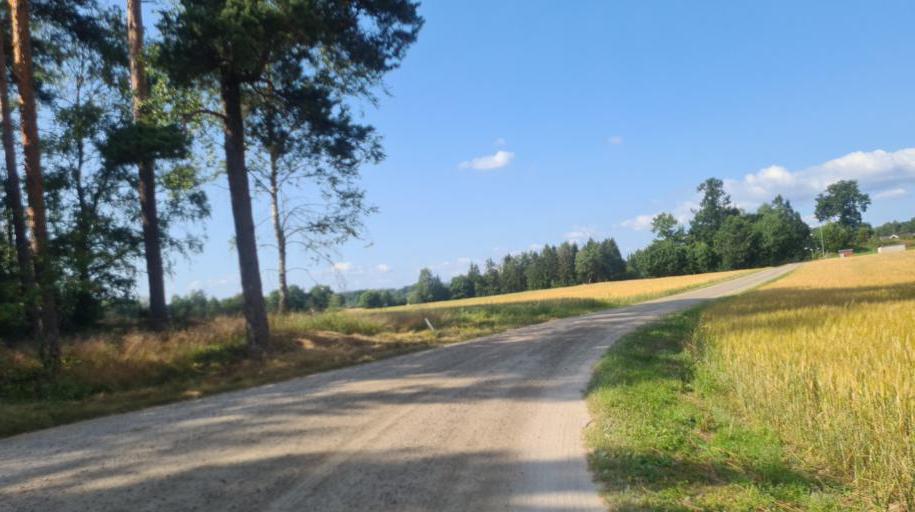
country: SE
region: Kronoberg
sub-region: Ljungby Kommun
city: Ljungby
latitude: 56.7315
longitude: 13.8709
